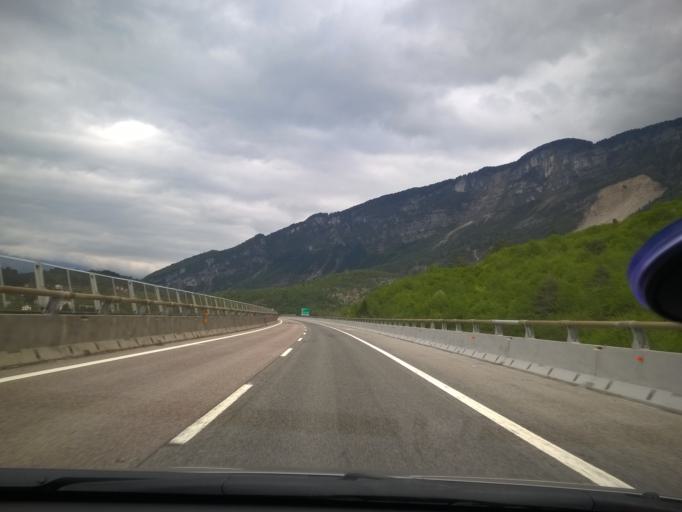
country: IT
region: Veneto
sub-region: Provincia di Treviso
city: Fregona
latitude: 46.0659
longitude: 12.3357
